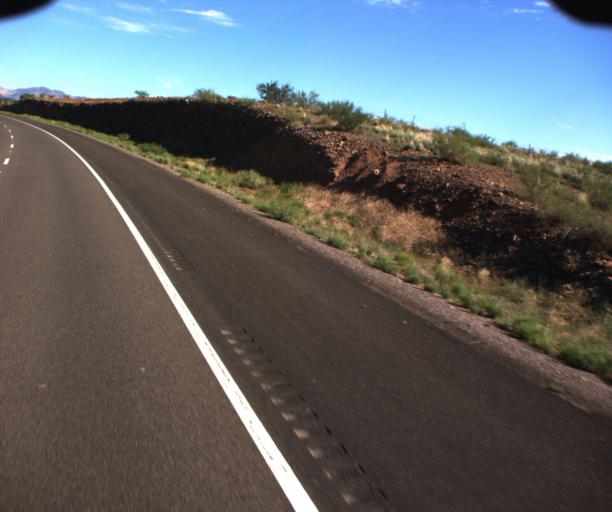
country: US
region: Arizona
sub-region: Greenlee County
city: Clifton
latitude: 32.9663
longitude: -109.2337
